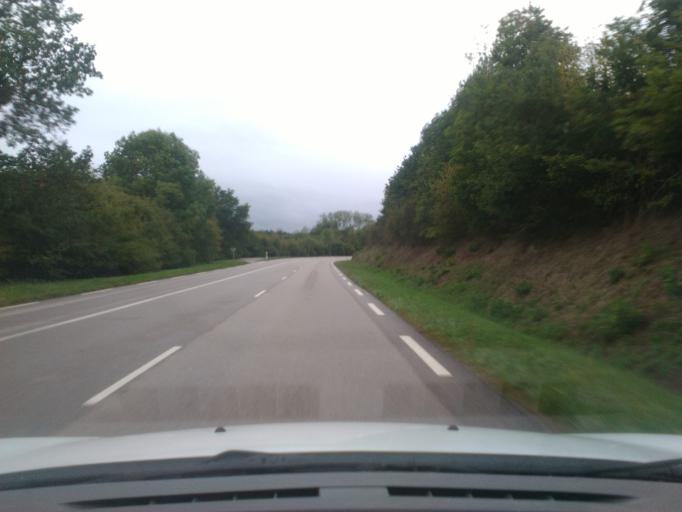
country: FR
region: Lorraine
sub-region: Departement des Vosges
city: Saint-Michel-sur-Meurthe
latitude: 48.3270
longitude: 6.8731
